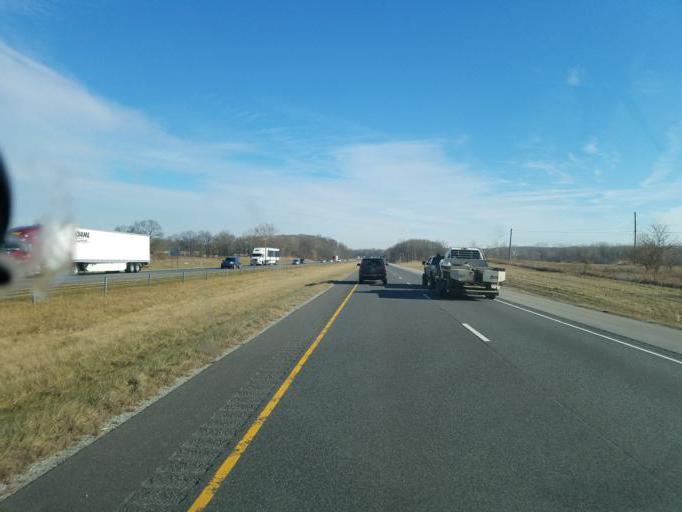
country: US
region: Indiana
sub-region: Henry County
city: Knightstown
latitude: 39.8491
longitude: -85.4941
